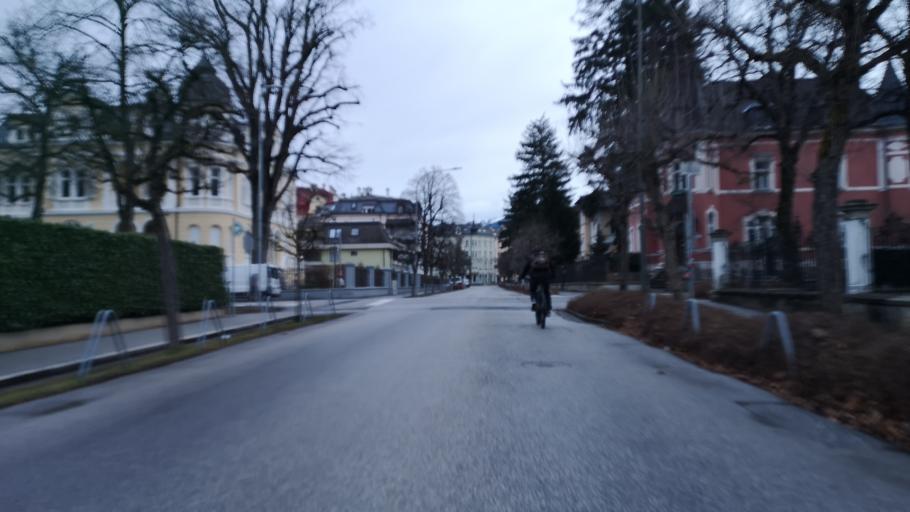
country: AT
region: Tyrol
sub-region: Innsbruck Stadt
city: Innsbruck
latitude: 47.2760
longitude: 11.4028
